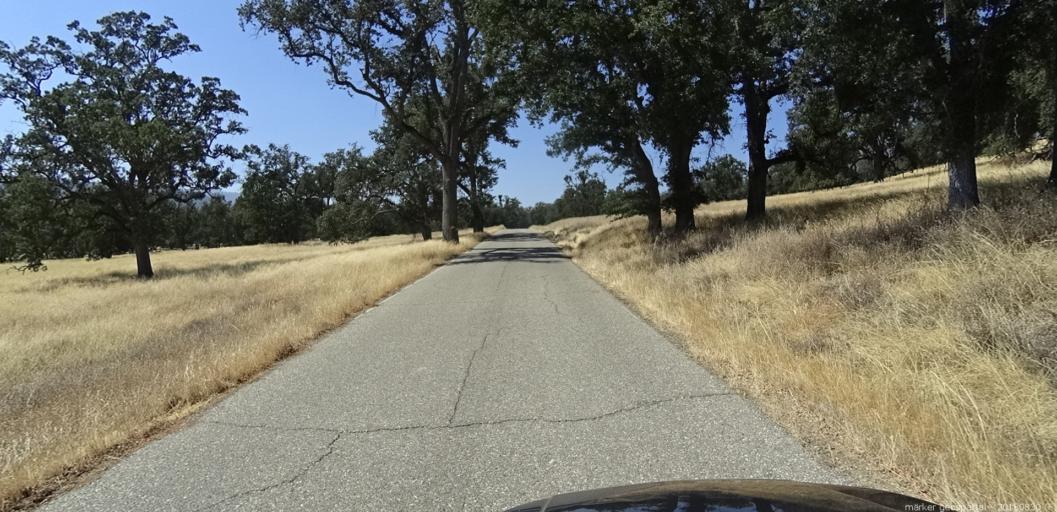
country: US
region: California
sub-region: Monterey County
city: Greenfield
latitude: 36.0776
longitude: -121.3796
